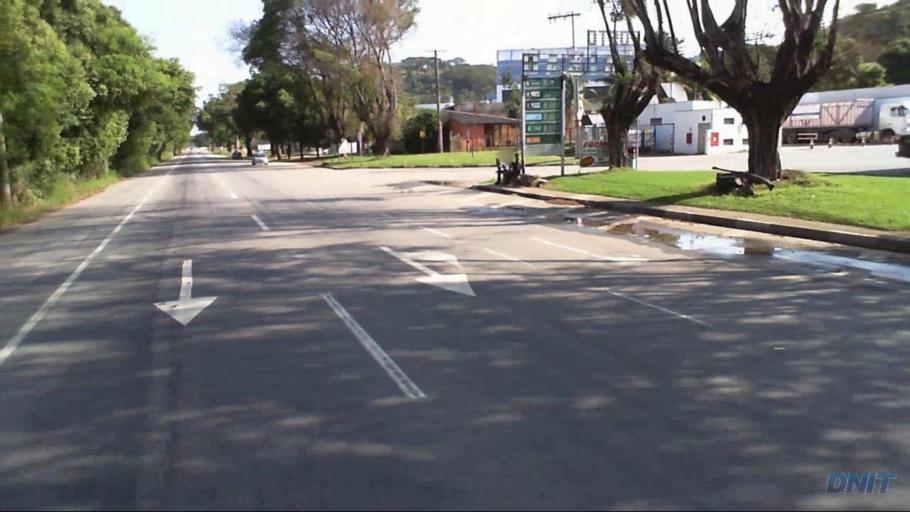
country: BR
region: Minas Gerais
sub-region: Ipatinga
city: Ipatinga
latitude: -19.4941
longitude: -42.5636
